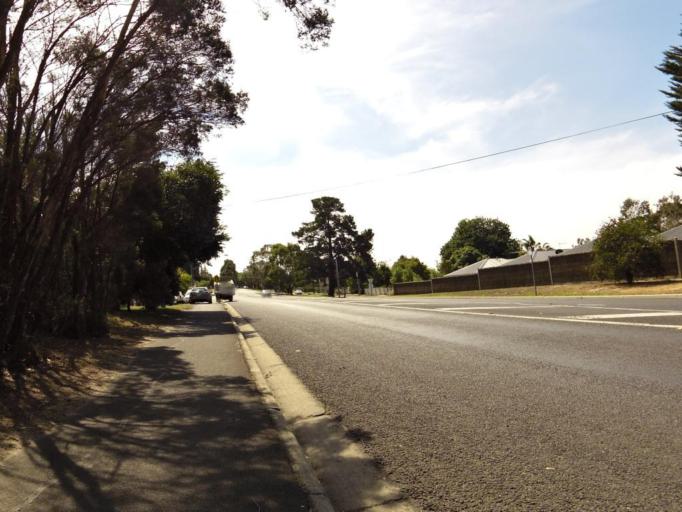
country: AU
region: Victoria
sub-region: Mornington Peninsula
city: Tyabb
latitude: -38.2312
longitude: 145.1824
